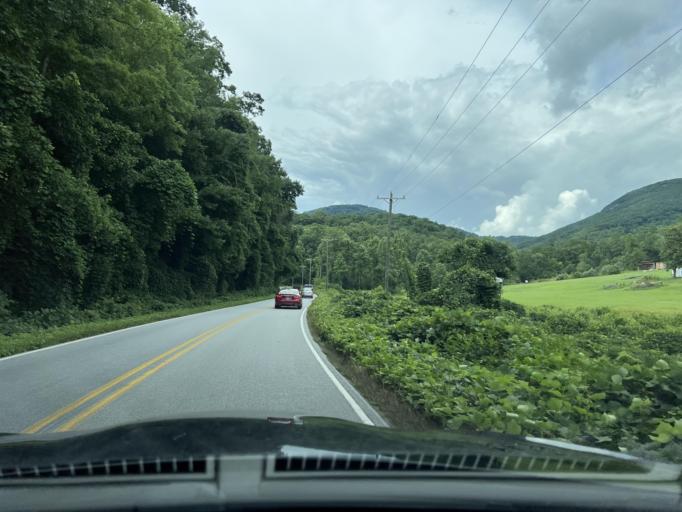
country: US
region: North Carolina
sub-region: Henderson County
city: Fruitland
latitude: 35.4114
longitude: -82.4100
